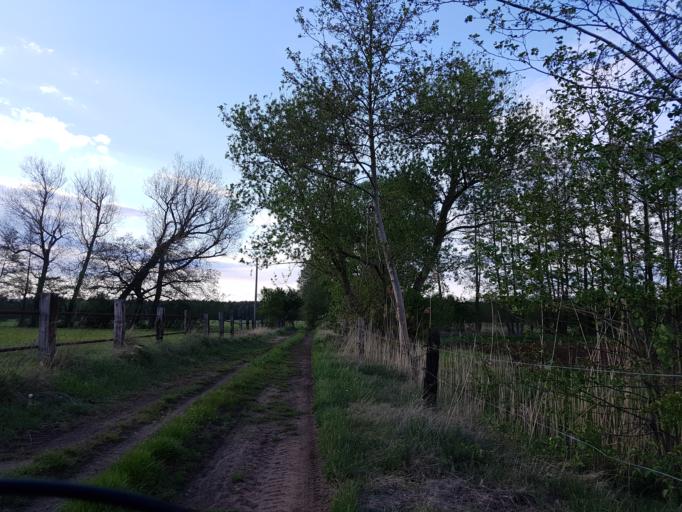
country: DE
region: Brandenburg
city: Schilda
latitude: 51.5800
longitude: 13.3655
